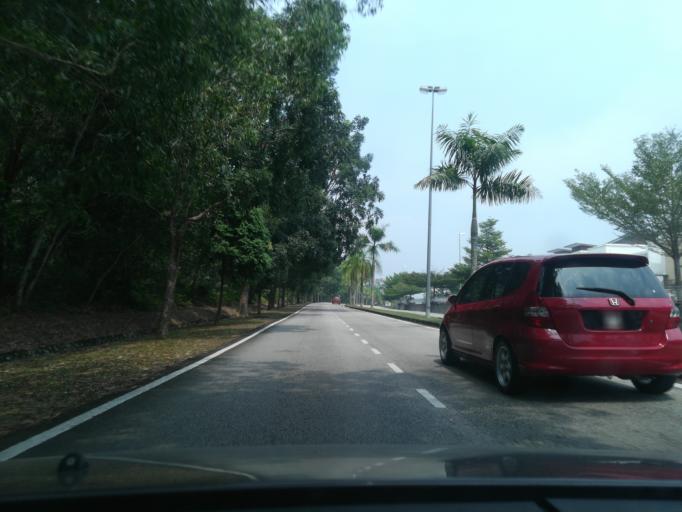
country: MY
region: Kedah
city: Kulim
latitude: 5.3989
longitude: 100.5785
